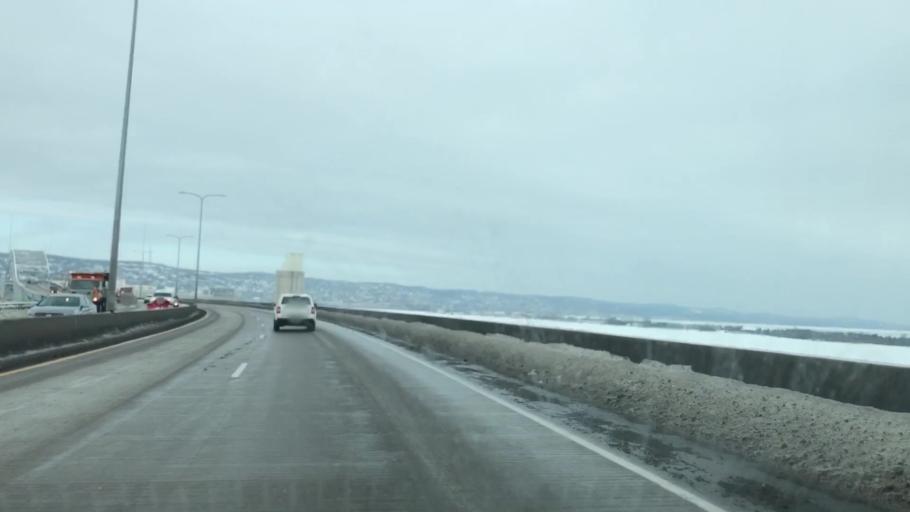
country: US
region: Wisconsin
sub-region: Douglas County
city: Superior
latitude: 46.7437
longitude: -92.0964
